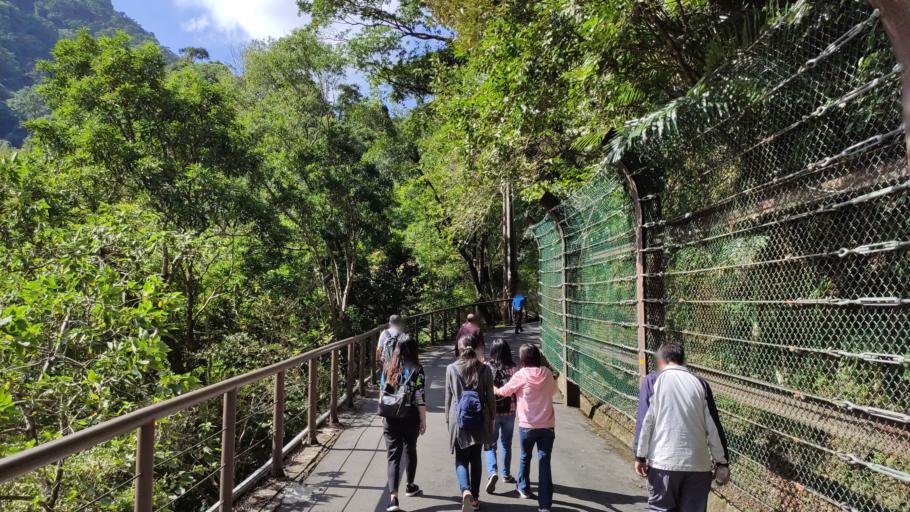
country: TW
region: Taiwan
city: Daxi
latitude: 24.8310
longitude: 121.4451
